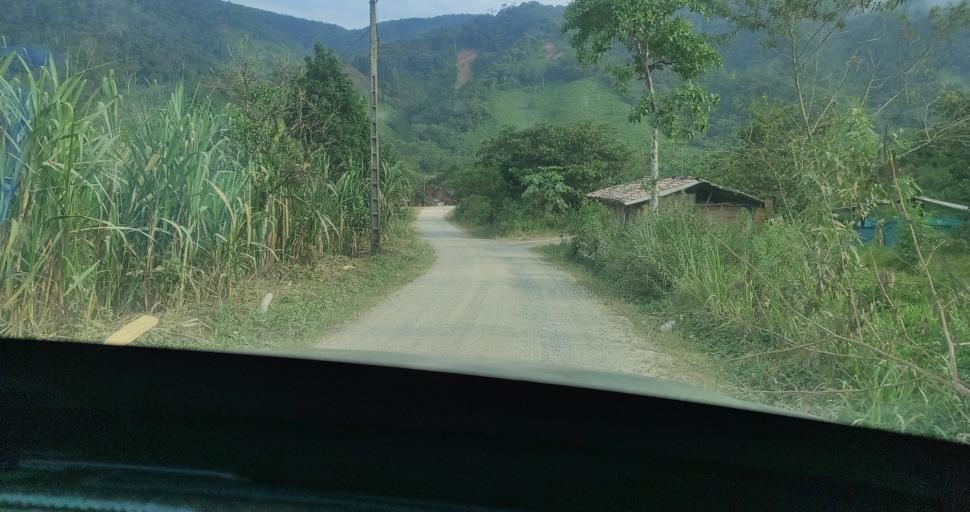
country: EC
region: Zamora-Chinchipe
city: Yantzaza
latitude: -3.7731
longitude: -78.8944
